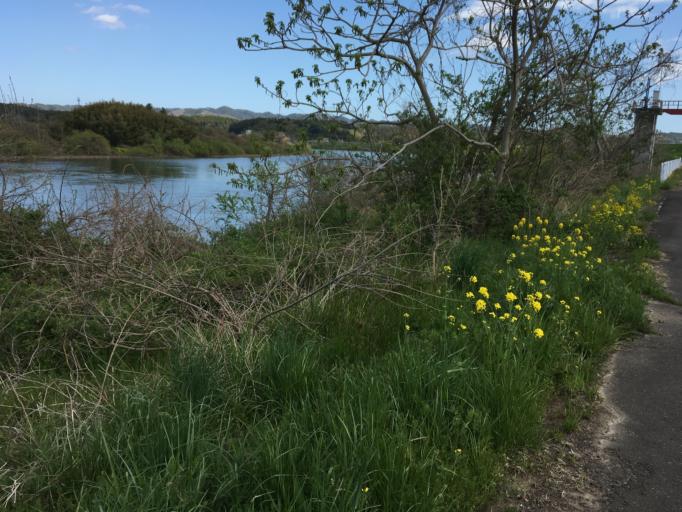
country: JP
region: Miyagi
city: Wakuya
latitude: 38.7099
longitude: 141.2667
